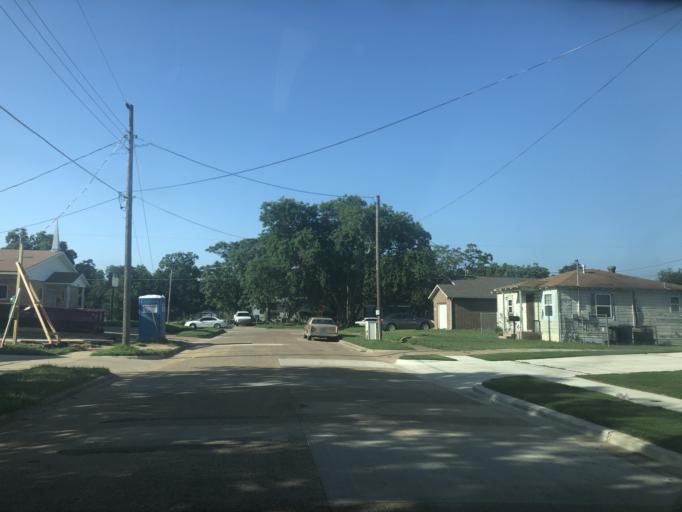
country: US
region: Texas
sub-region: Dallas County
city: Dallas
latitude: 32.7920
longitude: -96.8553
